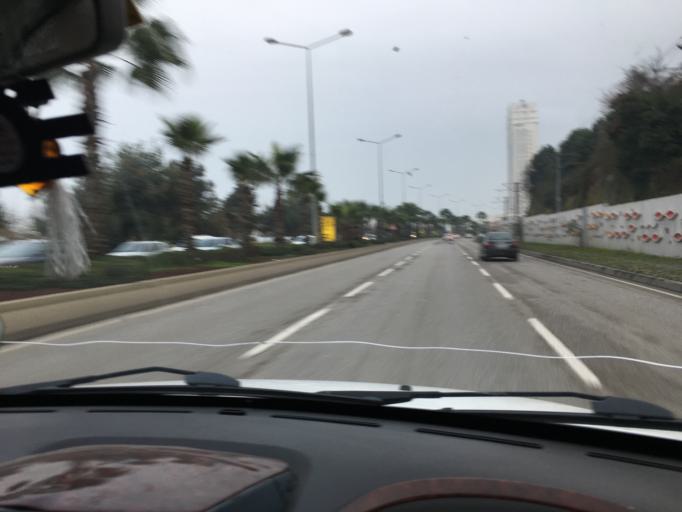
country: TR
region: Samsun
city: Samsun
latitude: 41.3170
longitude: 36.3328
